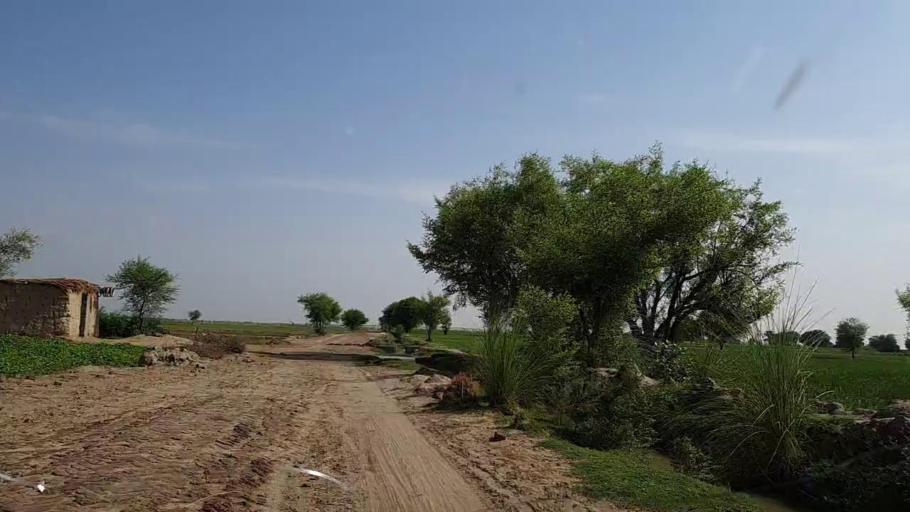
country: PK
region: Sindh
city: Khanpur
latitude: 27.6918
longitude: 69.3673
